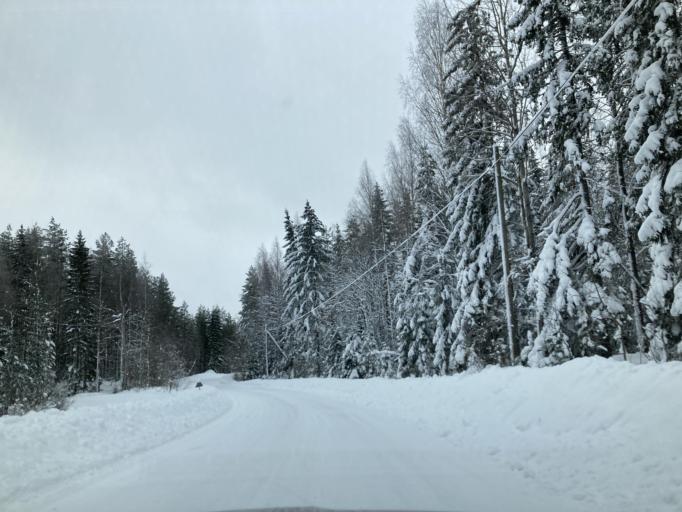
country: FI
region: Central Finland
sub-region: Jaemsae
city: Jaemsae
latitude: 61.8775
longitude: 25.3202
